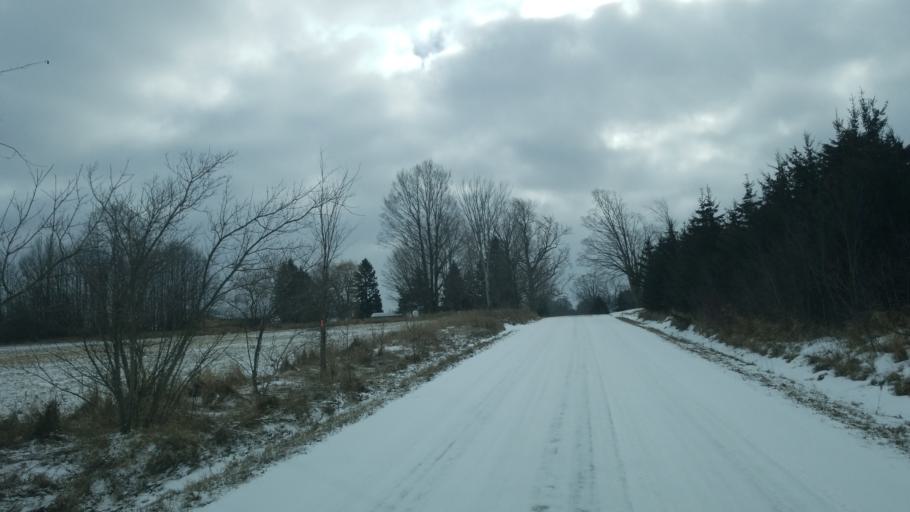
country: US
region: Michigan
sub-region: Osceola County
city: Evart
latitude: 44.0238
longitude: -85.2269
